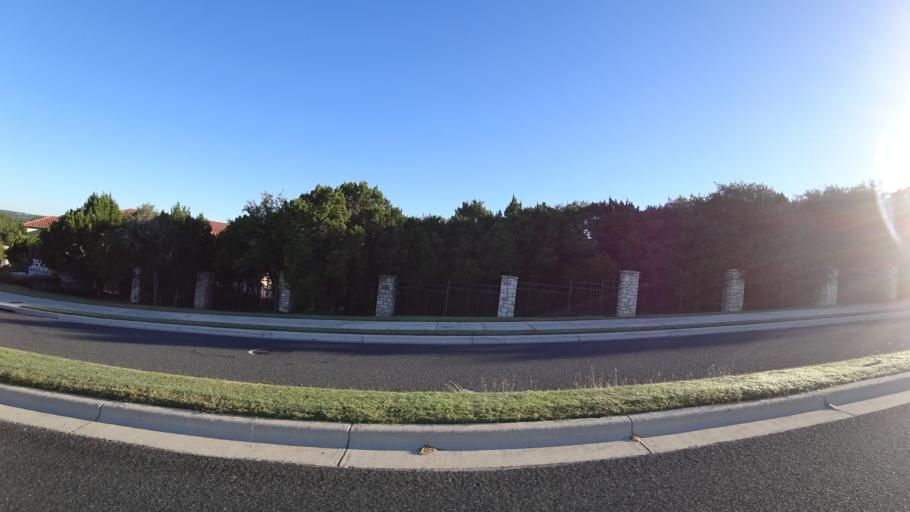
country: US
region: Texas
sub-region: Travis County
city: West Lake Hills
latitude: 30.3313
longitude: -97.8110
